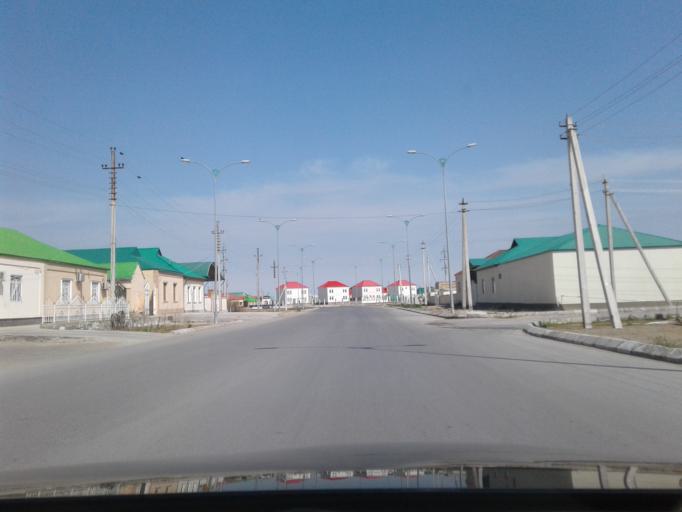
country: TM
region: Ahal
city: Ashgabat
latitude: 37.9895
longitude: 58.4035
